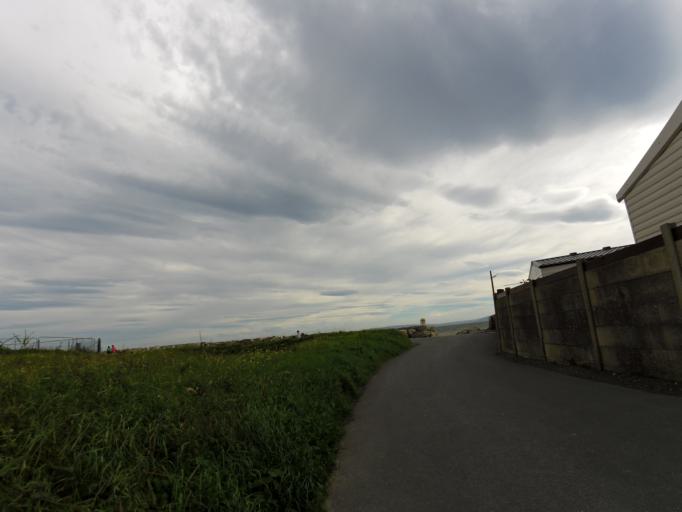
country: IE
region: Connaught
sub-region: County Galway
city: Bearna
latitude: 53.2562
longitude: -9.1047
